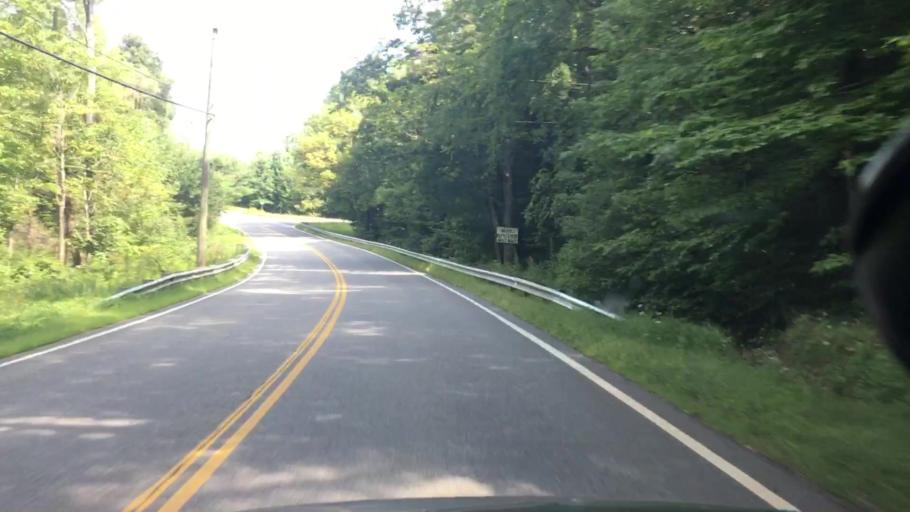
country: US
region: Massachusetts
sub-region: Franklin County
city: Shelburne
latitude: 42.6333
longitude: -72.6668
